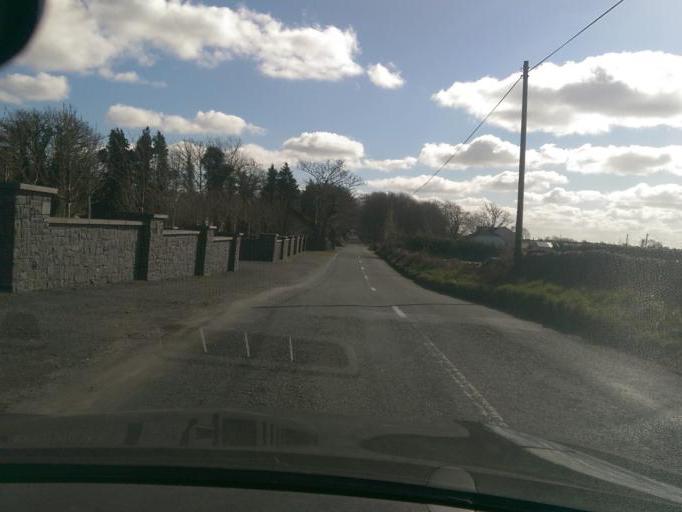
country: IE
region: Connaught
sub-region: County Galway
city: Athenry
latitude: 53.3405
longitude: -8.7741
